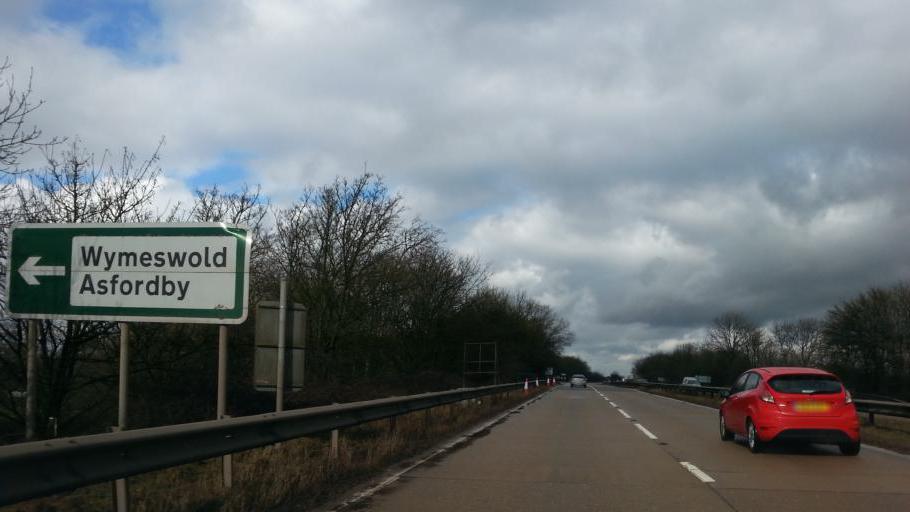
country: GB
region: England
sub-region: Leicestershire
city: Grimston
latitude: 52.7967
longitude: -1.0436
